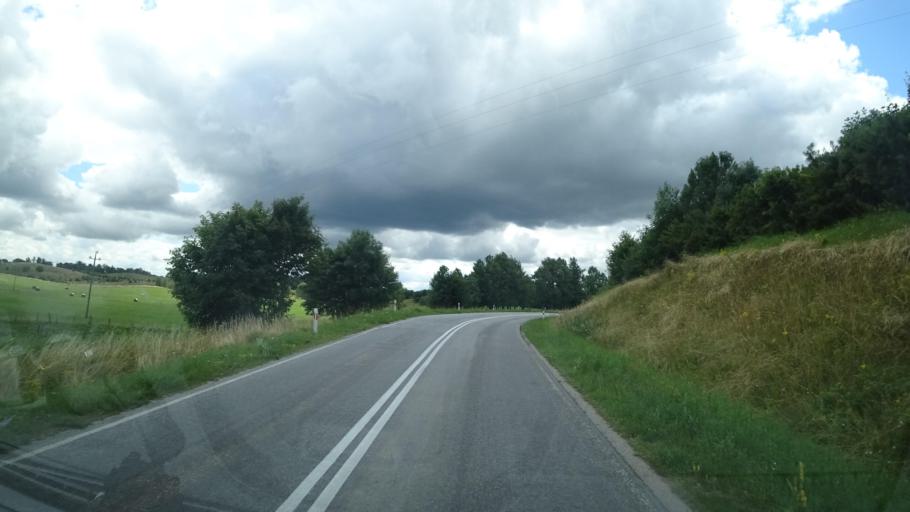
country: PL
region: Warmian-Masurian Voivodeship
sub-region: Powiat goldapski
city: Goldap
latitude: 54.2195
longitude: 22.2296
